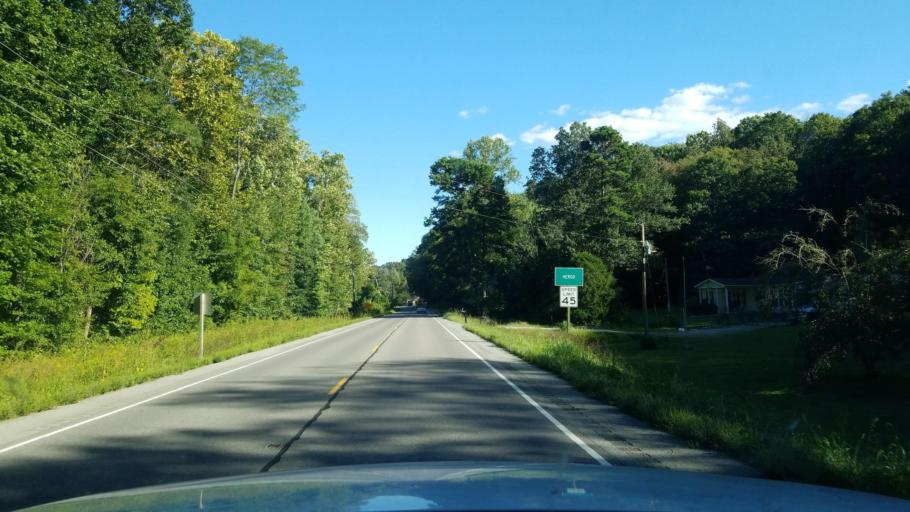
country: US
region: Illinois
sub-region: Saline County
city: Harrisburg
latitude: 37.5847
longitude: -88.4430
